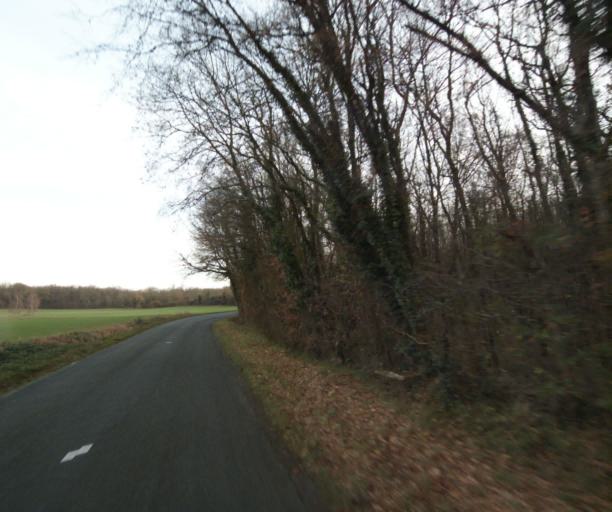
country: FR
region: Poitou-Charentes
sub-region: Departement de la Charente-Maritime
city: Fontcouverte
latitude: 45.8084
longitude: -0.5833
